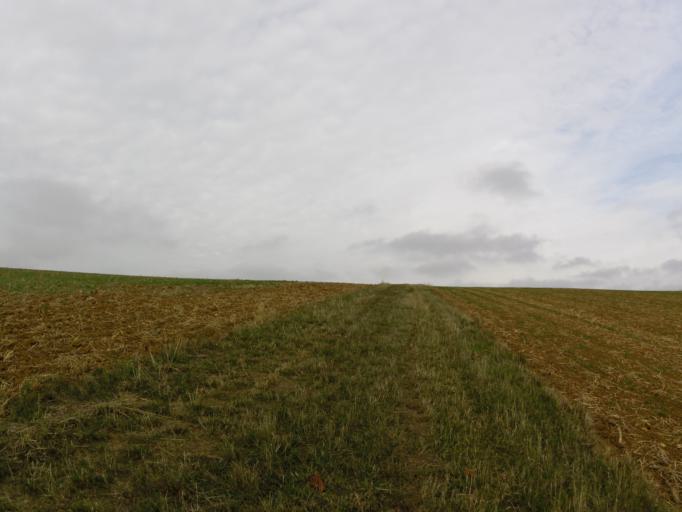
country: DE
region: Bavaria
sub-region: Regierungsbezirk Unterfranken
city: Waldbrunn
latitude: 49.7547
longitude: 9.8033
